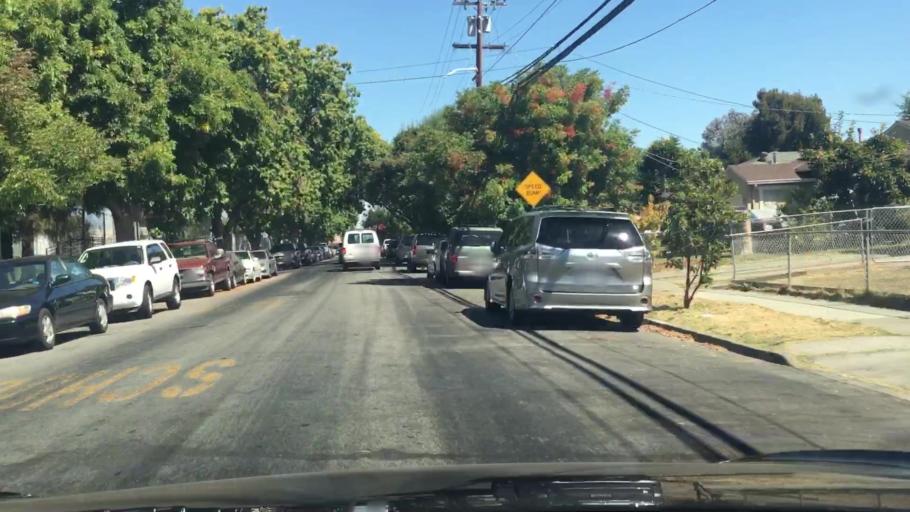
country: US
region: California
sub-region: San Mateo County
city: North Fair Oaks
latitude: 37.4819
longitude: -122.2144
